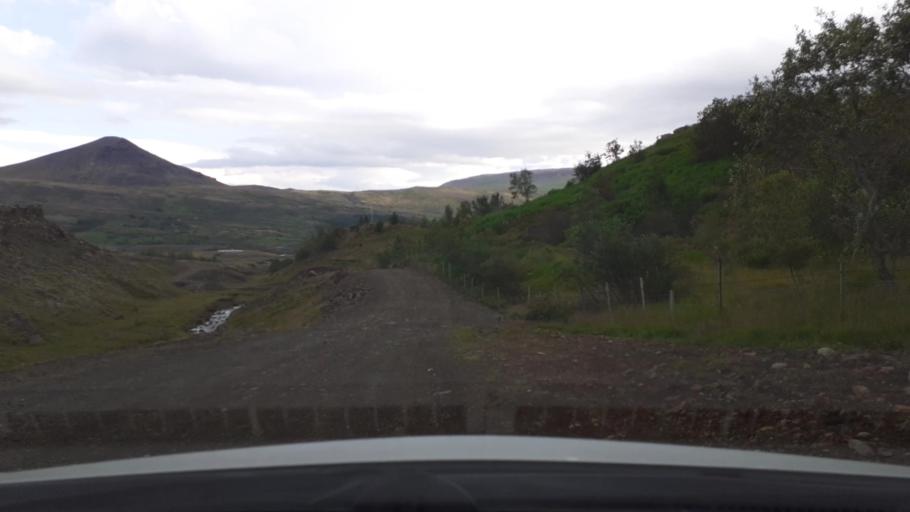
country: IS
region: Capital Region
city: Mosfellsbaer
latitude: 64.2841
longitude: -21.4635
